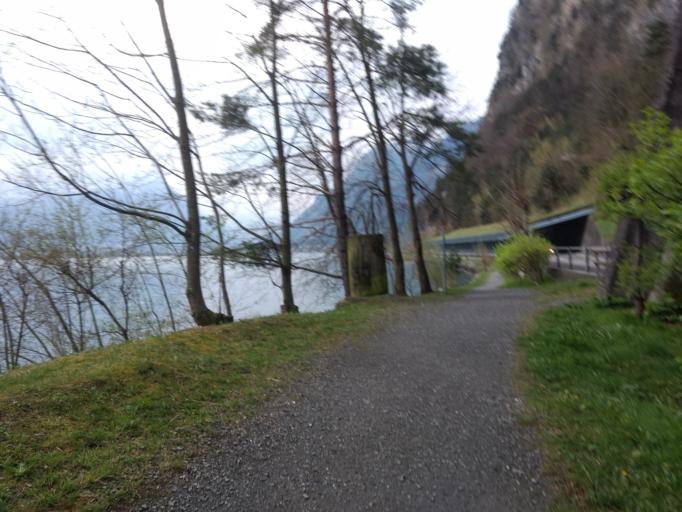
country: CH
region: Uri
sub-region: Uri
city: Bauen
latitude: 46.9138
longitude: 8.5919
